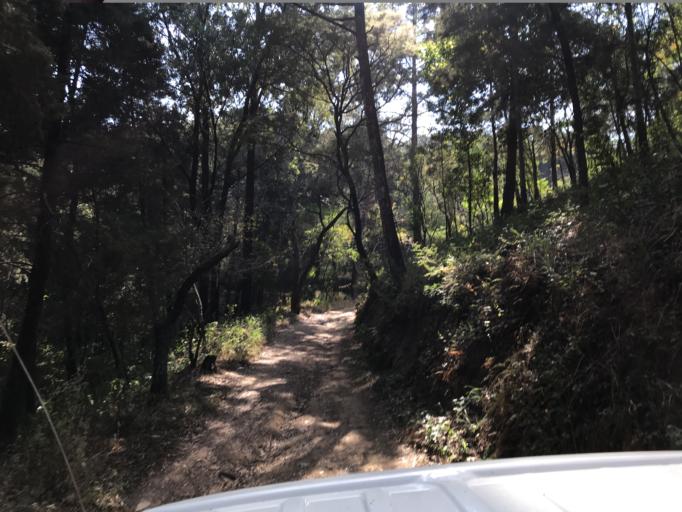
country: GT
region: Guatemala
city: Villa Canales
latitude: 14.4821
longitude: -90.5507
